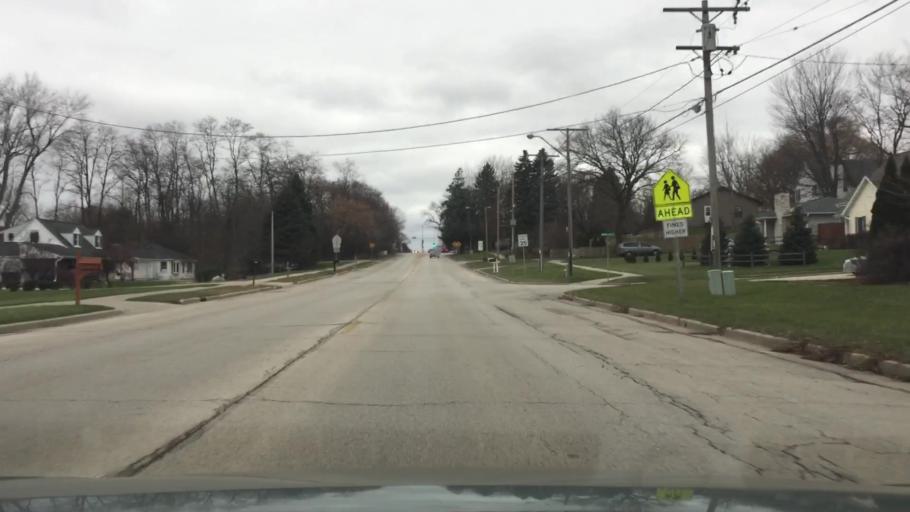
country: US
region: Wisconsin
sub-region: Waukesha County
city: Waukesha
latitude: 43.0217
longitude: -88.2647
